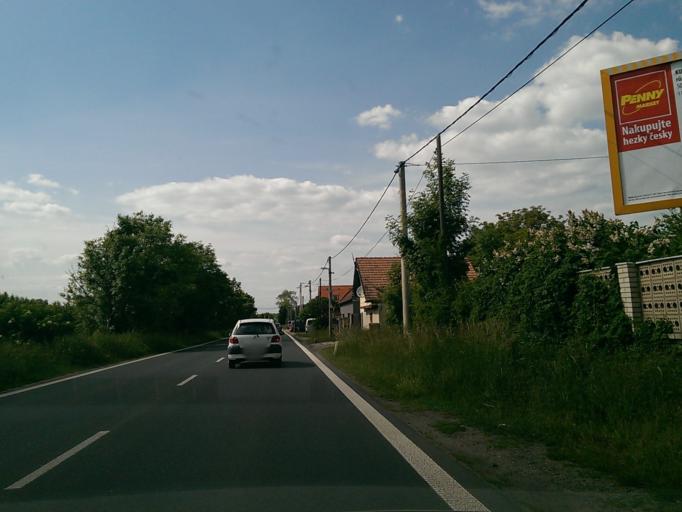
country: CZ
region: Central Bohemia
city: Libis
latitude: 50.3175
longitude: 14.5109
